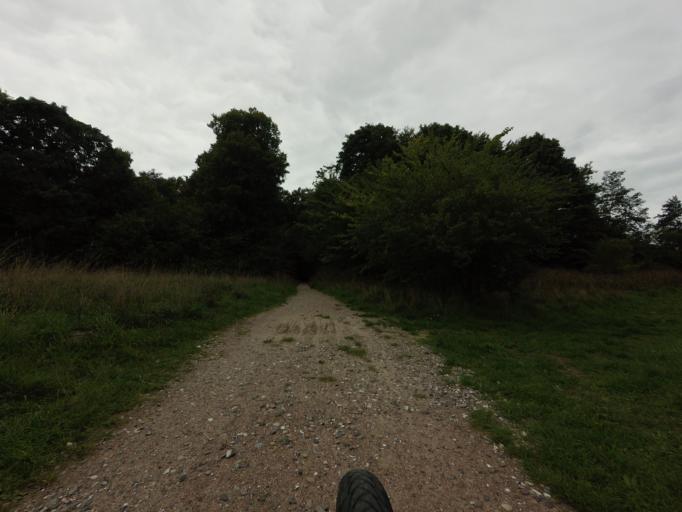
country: DK
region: North Denmark
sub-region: Hjorring Kommune
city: Sindal
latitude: 57.5829
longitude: 10.1841
